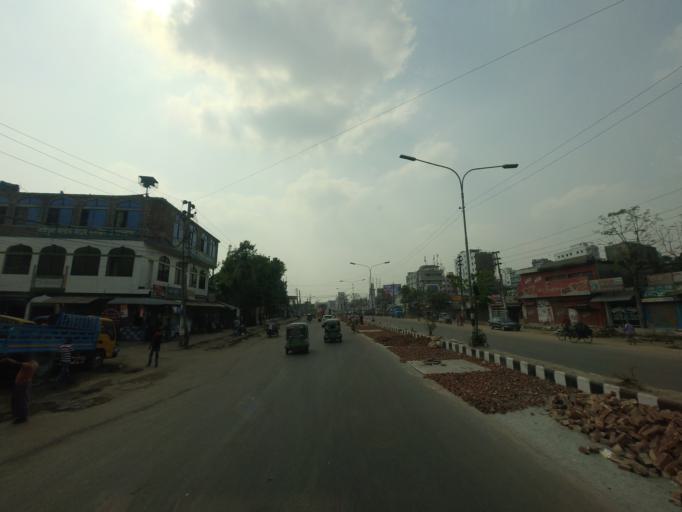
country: BD
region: Dhaka
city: Azimpur
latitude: 23.7827
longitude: 90.3483
